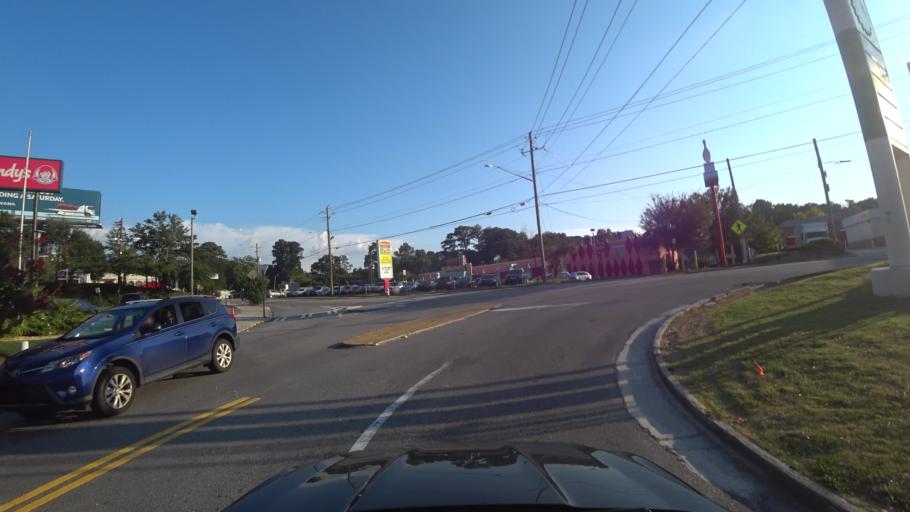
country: US
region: Georgia
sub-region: DeKalb County
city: Druid Hills
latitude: 33.8105
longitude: -84.3678
